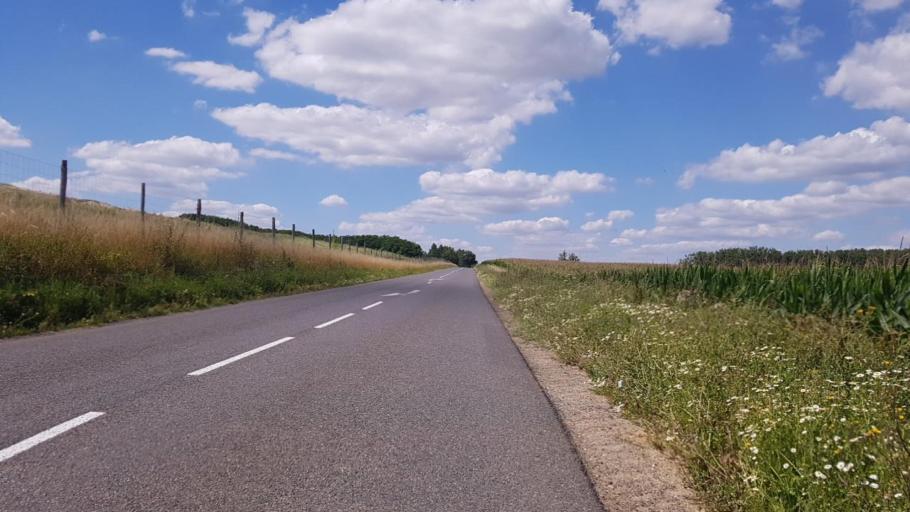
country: FR
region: Ile-de-France
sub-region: Departement de Seine-et-Marne
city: Moussy-le-Vieux
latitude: 49.0241
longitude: 2.6446
